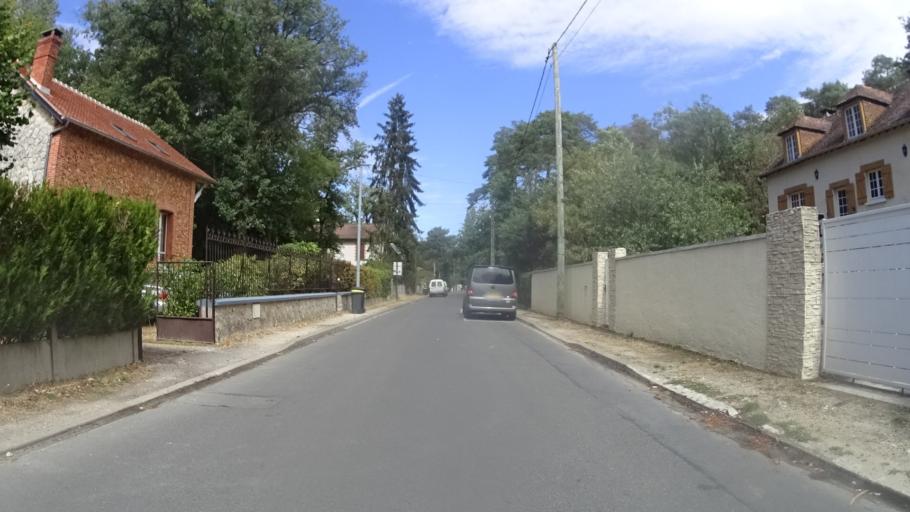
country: FR
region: Centre
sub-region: Departement du Loiret
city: Malesherbes
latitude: 48.2897
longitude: 2.4306
